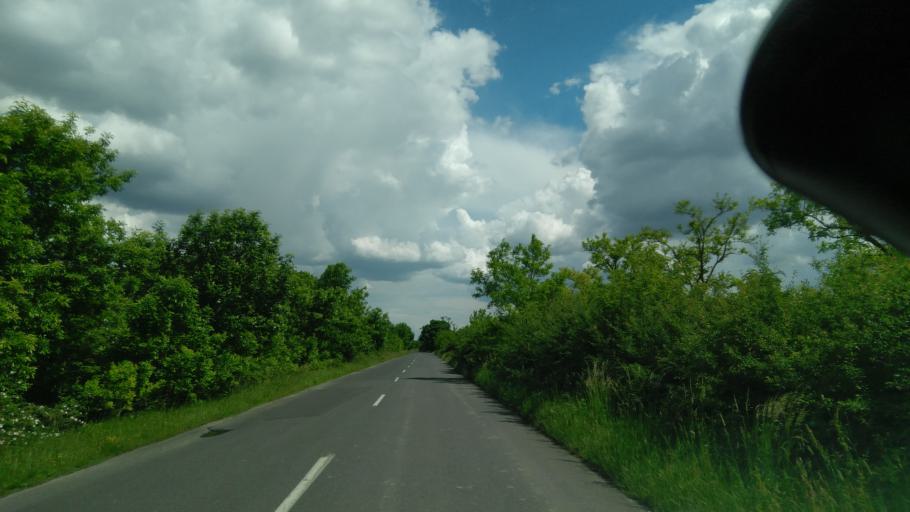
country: HU
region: Bekes
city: Korosladany
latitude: 46.9822
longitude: 21.0465
